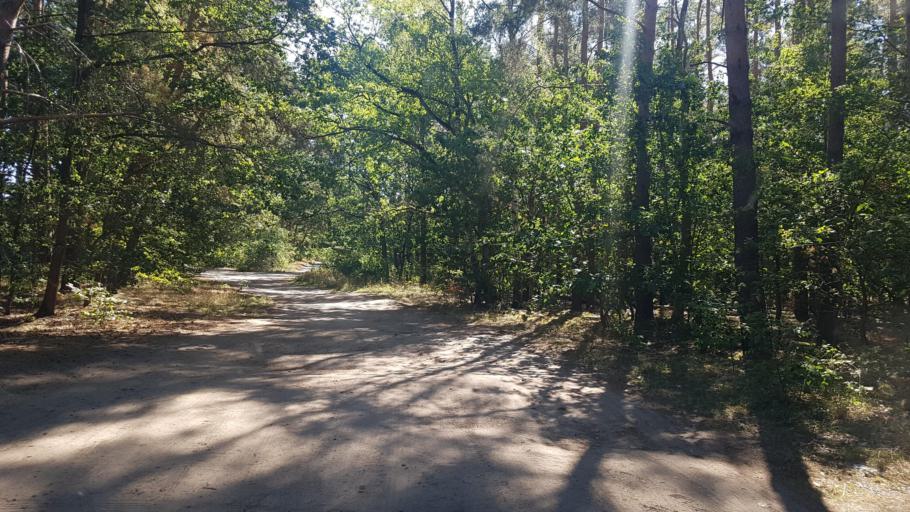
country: DE
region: Brandenburg
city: Brandenburg an der Havel
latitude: 52.3463
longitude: 12.5219
